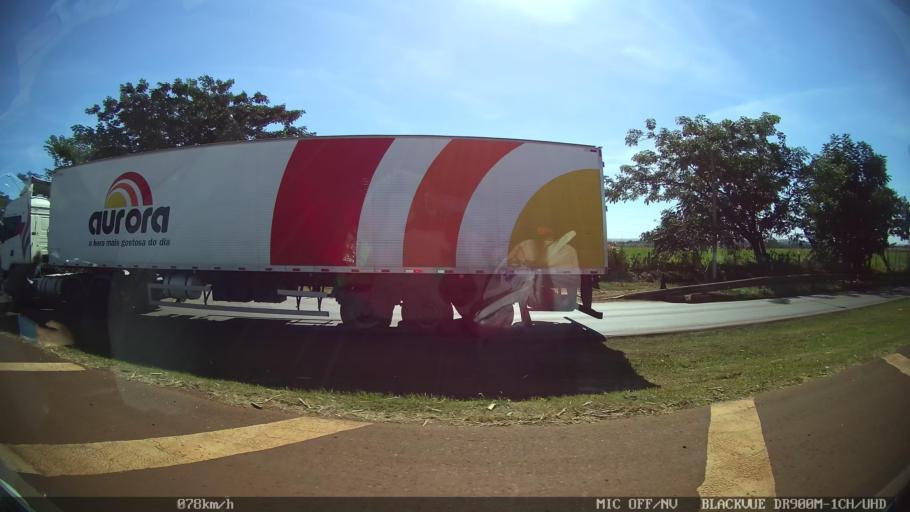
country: BR
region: Sao Paulo
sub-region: Barretos
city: Barretos
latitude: -20.4853
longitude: -48.5123
